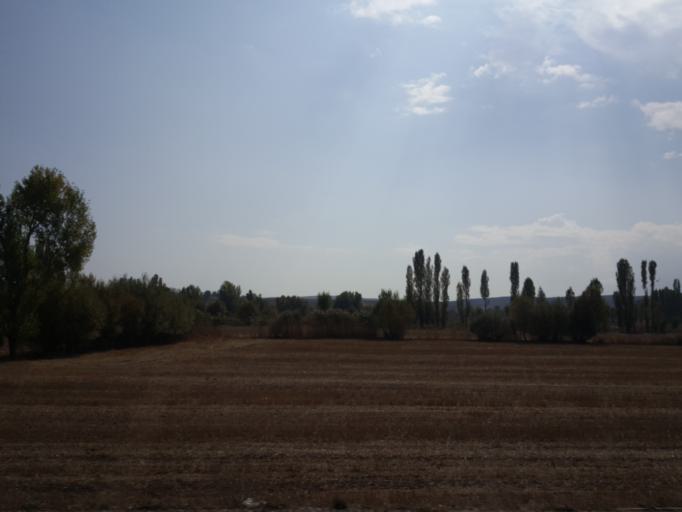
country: TR
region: Corum
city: Alaca
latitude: 40.1506
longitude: 34.8482
